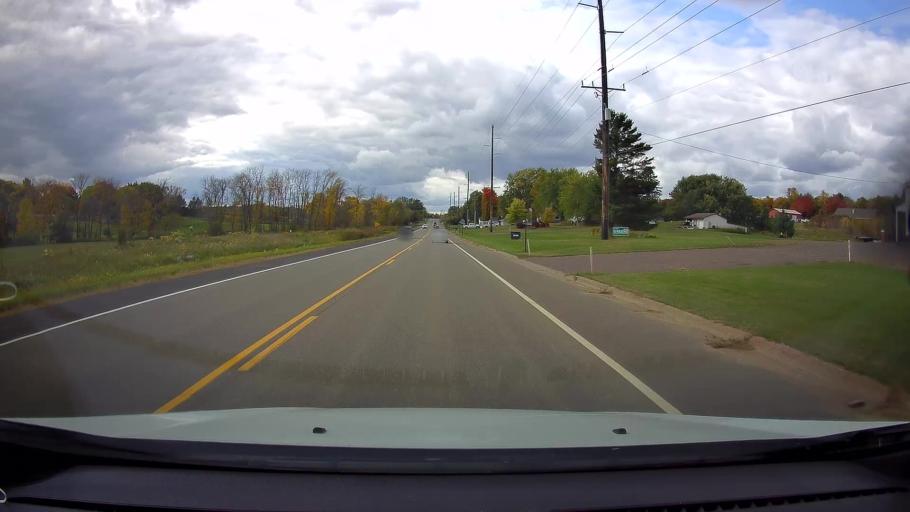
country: US
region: Minnesota
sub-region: Chisago County
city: Center City
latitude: 45.3973
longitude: -92.8009
